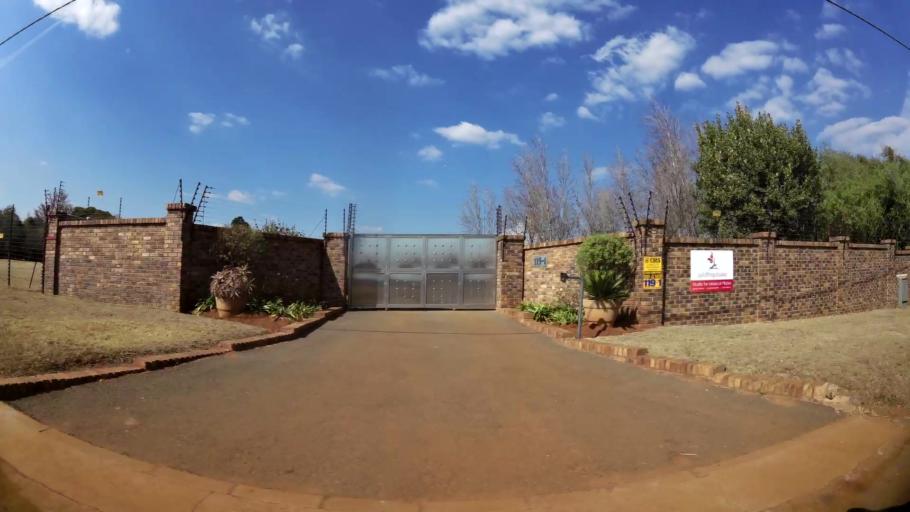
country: ZA
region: Gauteng
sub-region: Ekurhuleni Metropolitan Municipality
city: Benoni
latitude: -26.0820
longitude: 28.3273
